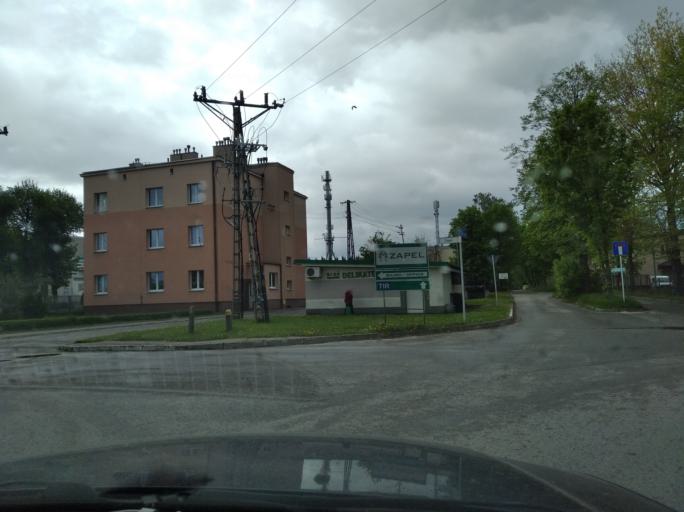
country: PL
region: Subcarpathian Voivodeship
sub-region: Powiat rzeszowski
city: Boguchwala
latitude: 49.9889
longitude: 21.9355
